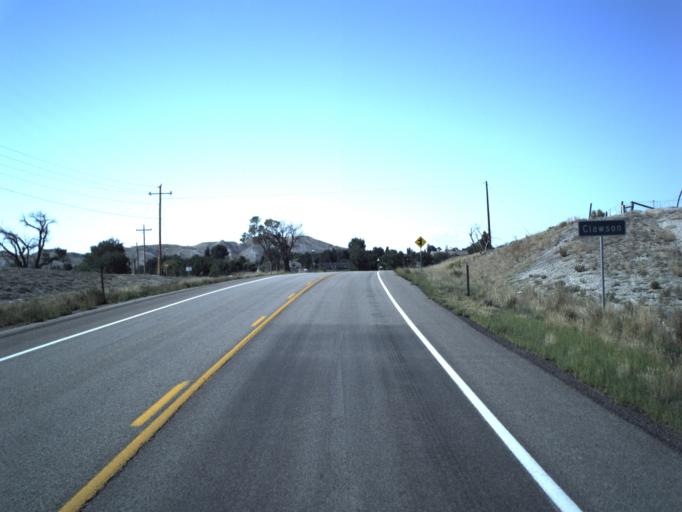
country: US
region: Utah
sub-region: Emery County
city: Ferron
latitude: 39.1394
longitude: -111.0968
